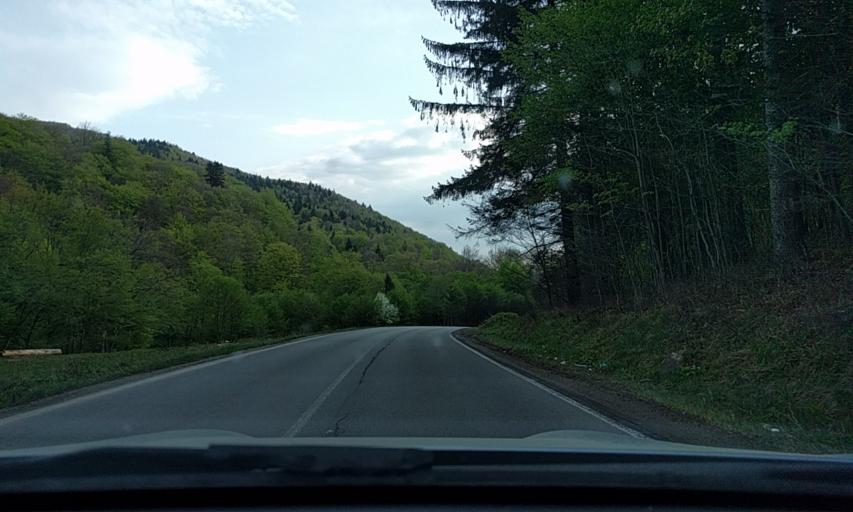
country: RO
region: Covasna
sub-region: Comuna Bretcu
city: Bretcu
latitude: 46.1084
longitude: 26.4120
